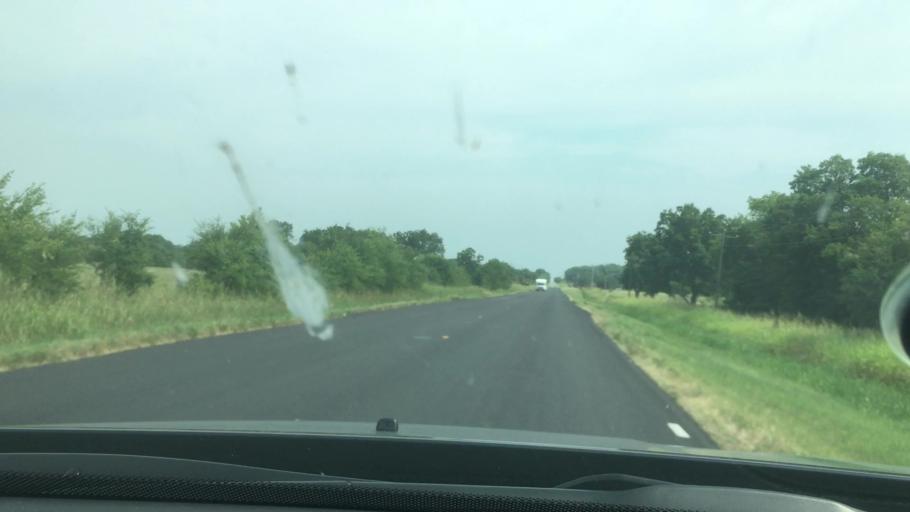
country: US
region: Oklahoma
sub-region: Coal County
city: Coalgate
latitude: 34.3538
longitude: -96.4246
